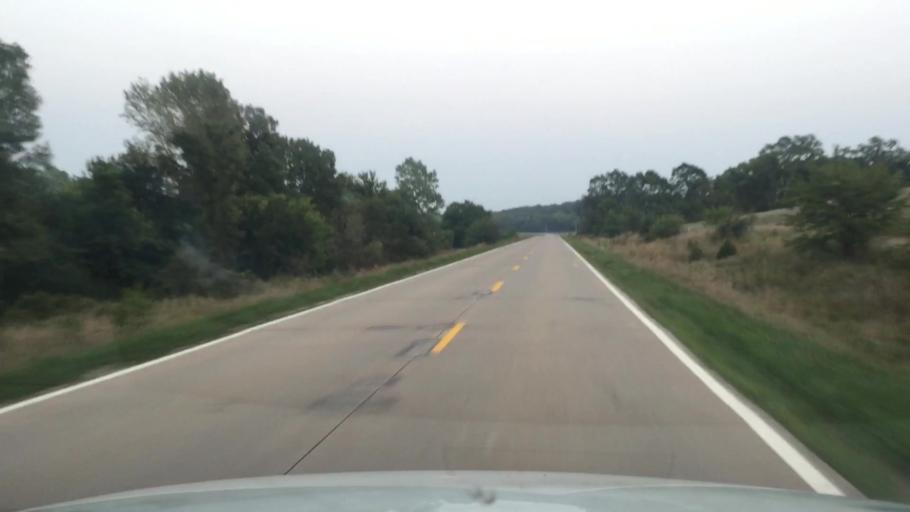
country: US
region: Iowa
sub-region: Warren County
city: Indianola
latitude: 41.1892
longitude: -93.6278
